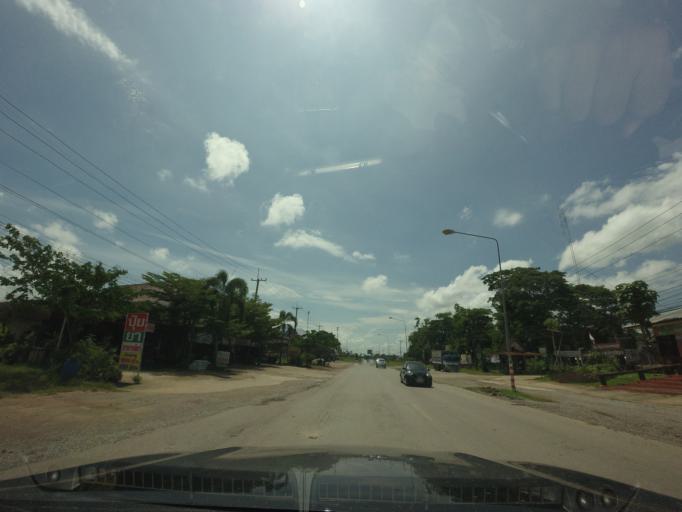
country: TH
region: Nong Khai
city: Pho Tak
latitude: 17.7760
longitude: 102.3953
